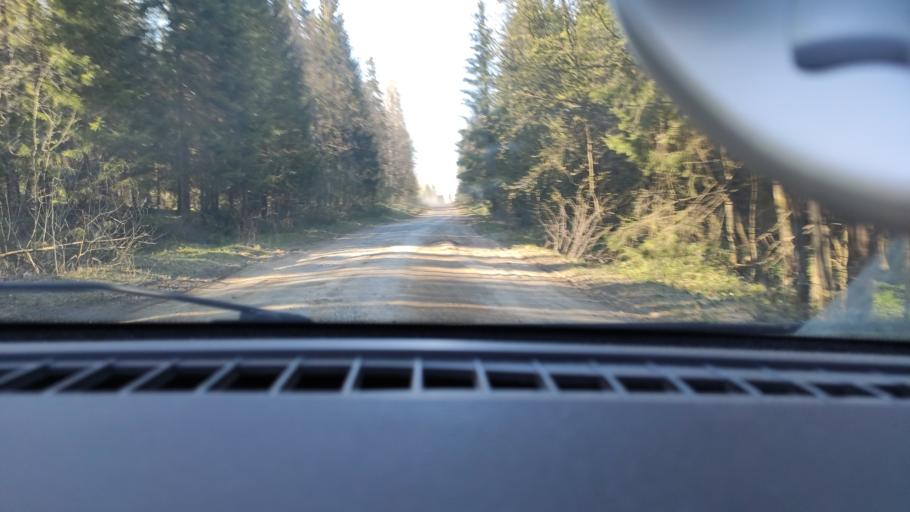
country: RU
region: Perm
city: Polazna
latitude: 58.1304
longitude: 56.4578
